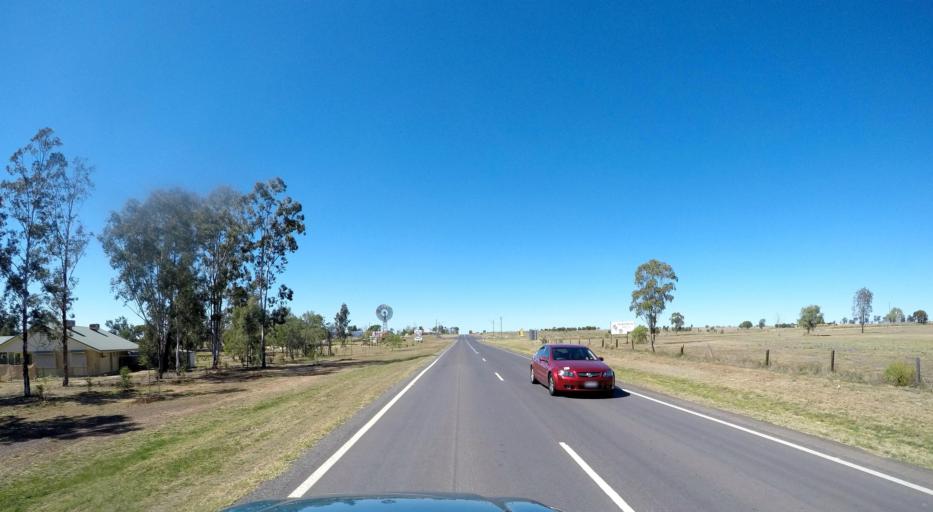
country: AU
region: Queensland
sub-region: Banana
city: Taroom
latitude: -26.1206
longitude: 149.9566
